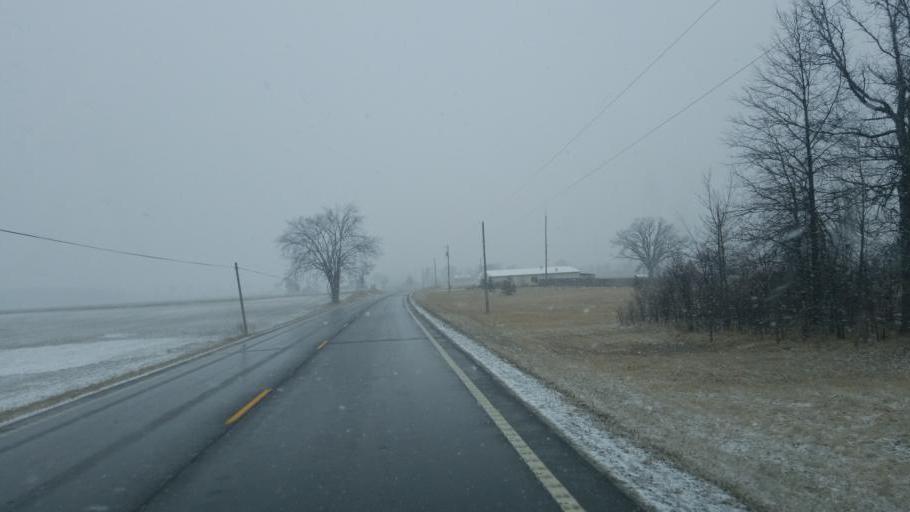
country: US
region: Ohio
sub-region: Defiance County
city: Hicksville
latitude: 41.3374
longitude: -84.7478
